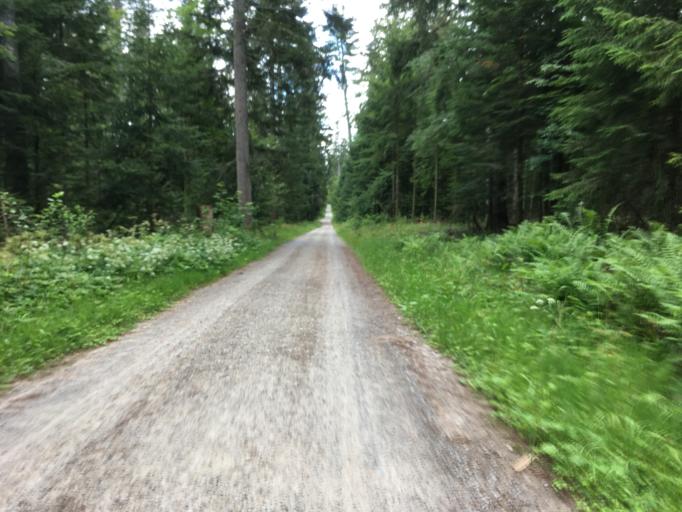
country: DE
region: Baden-Wuerttemberg
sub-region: Karlsruhe Region
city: Freudenstadt
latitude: 48.4480
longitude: 8.4089
